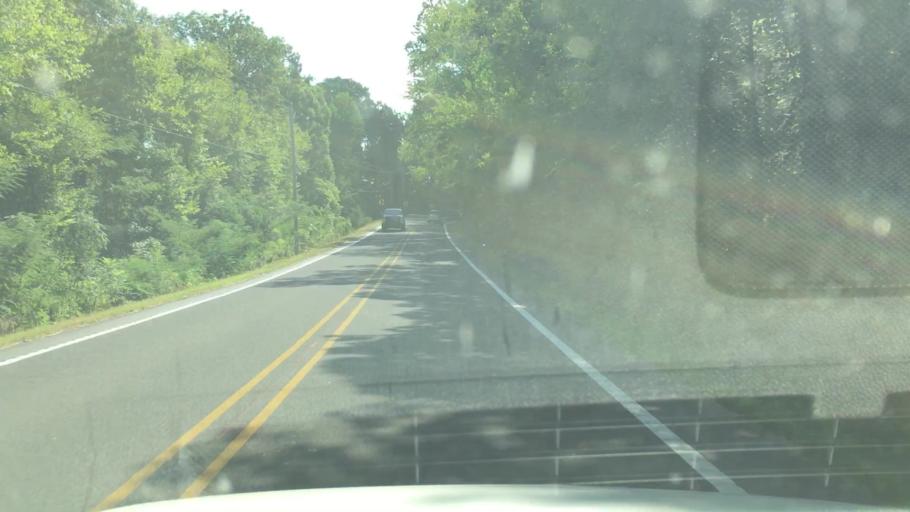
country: US
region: Arkansas
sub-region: Garland County
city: Piney
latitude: 34.5098
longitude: -93.1708
